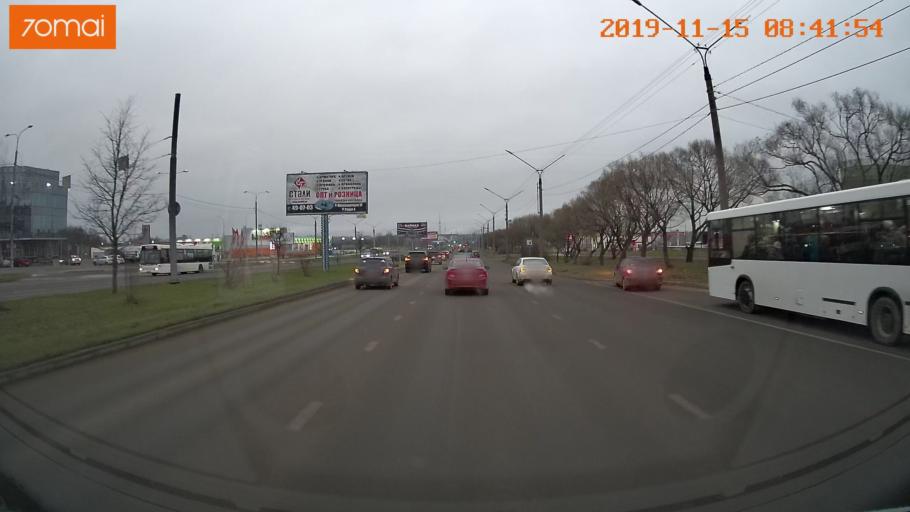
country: RU
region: Vologda
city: Cherepovets
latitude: 59.0989
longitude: 37.9107
